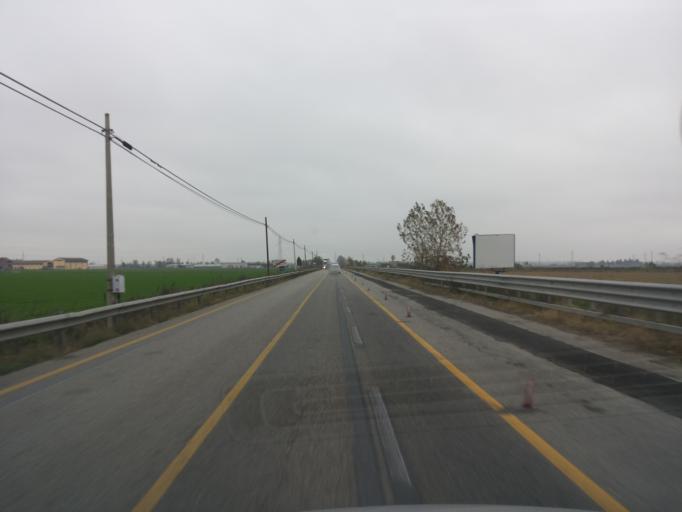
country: IT
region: Piedmont
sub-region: Provincia di Novara
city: Lumellogno
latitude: 45.4087
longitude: 8.5574
